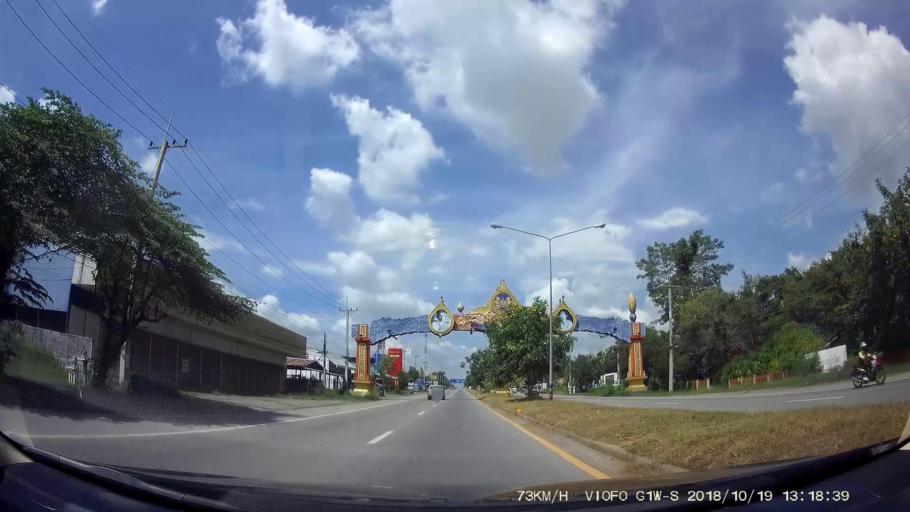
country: TH
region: Chaiyaphum
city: Chatturat
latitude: 15.4182
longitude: 101.8328
